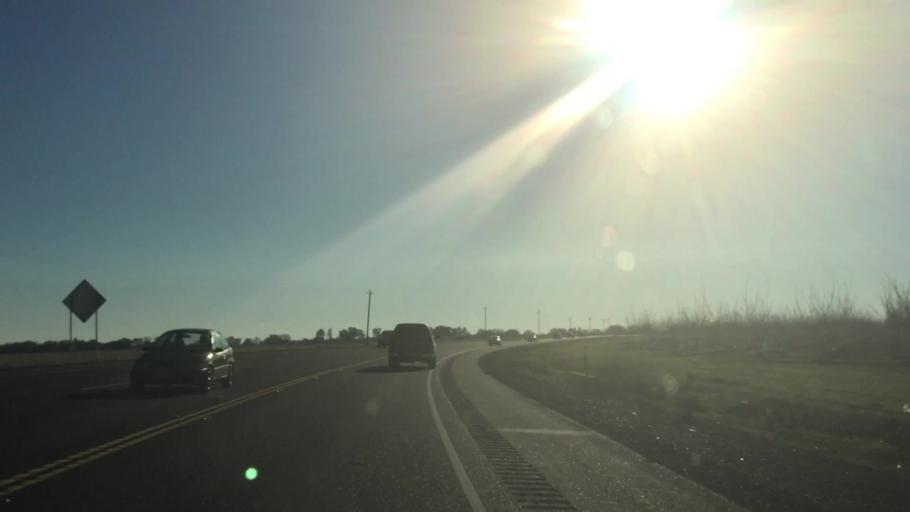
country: US
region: California
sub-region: Butte County
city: Palermo
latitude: 39.3913
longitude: -121.6063
